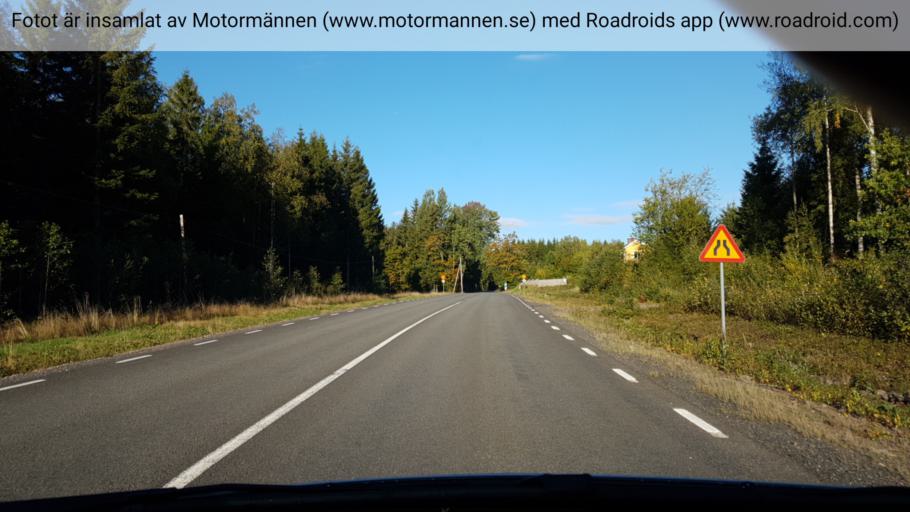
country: SE
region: Vaestra Goetaland
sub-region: Skovde Kommun
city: Stopen
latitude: 58.5366
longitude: 13.7334
